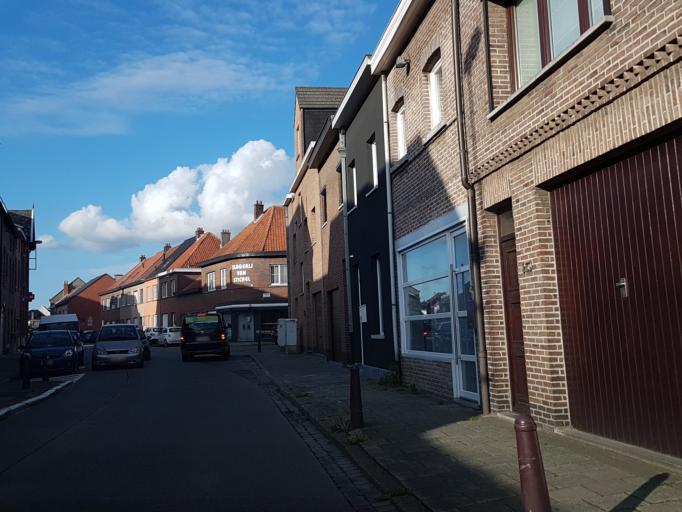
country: BE
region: Flanders
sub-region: Provincie Oost-Vlaanderen
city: Aalst
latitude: 50.9486
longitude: 4.0533
